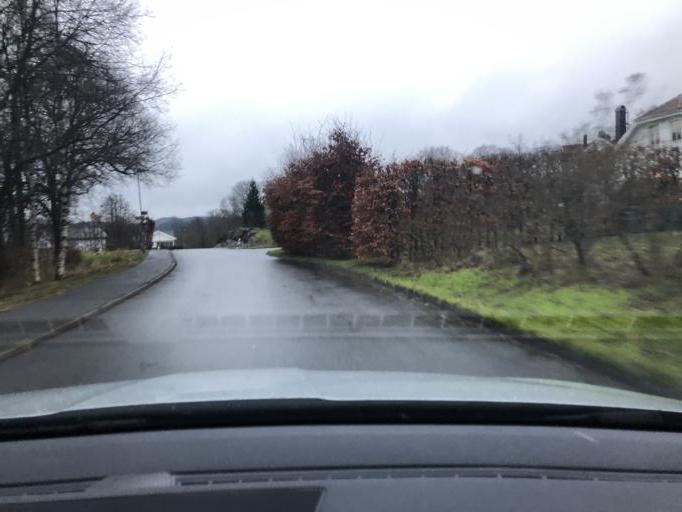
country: SE
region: Vaestra Goetaland
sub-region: Harryda Kommun
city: Landvetter
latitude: 57.6901
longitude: 12.1971
